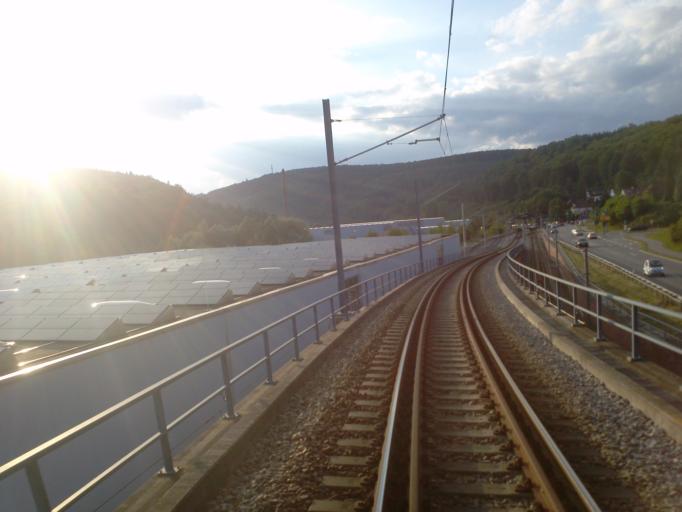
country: DE
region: Baden-Wuerttemberg
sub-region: Karlsruhe Region
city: Ettlingen
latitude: 48.9266
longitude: 8.4528
